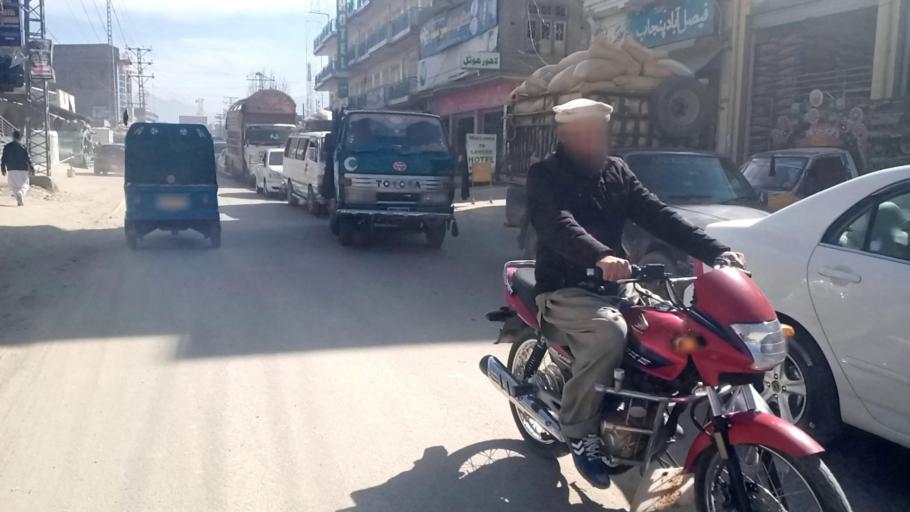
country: PK
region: Khyber Pakhtunkhwa
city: Mingora
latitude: 34.7890
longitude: 72.3490
